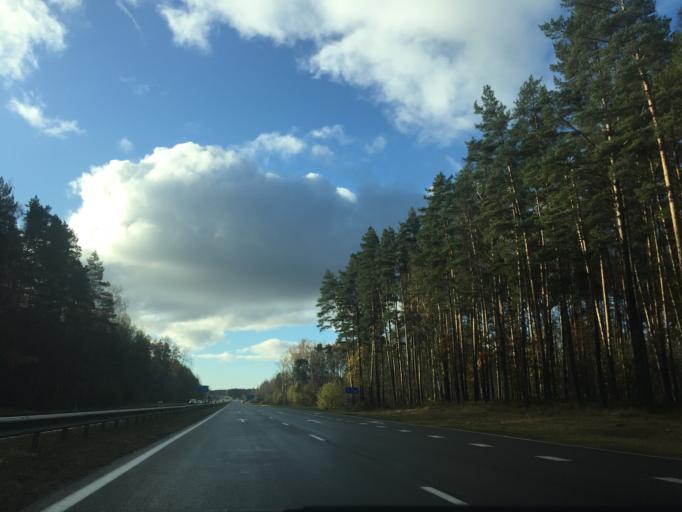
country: LV
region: Babite
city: Pinki
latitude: 56.9370
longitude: 23.9188
